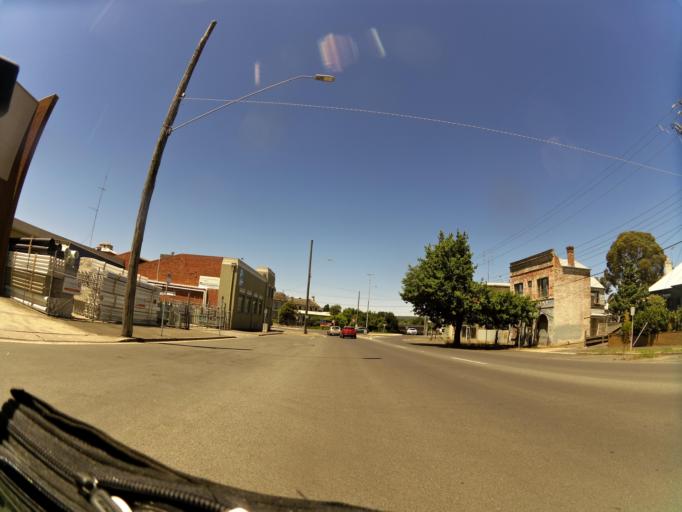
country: AU
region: Victoria
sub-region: Ballarat North
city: Ballarat
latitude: -37.5659
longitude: 143.8547
